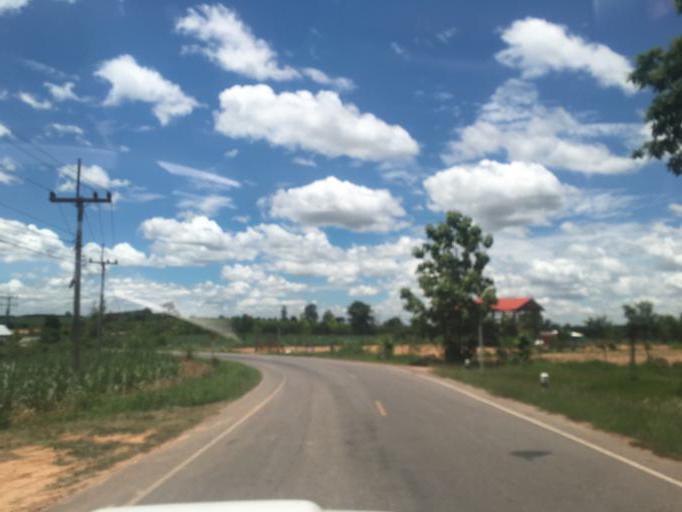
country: TH
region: Changwat Udon Thani
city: Nong Saeng
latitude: 17.2036
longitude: 102.7498
